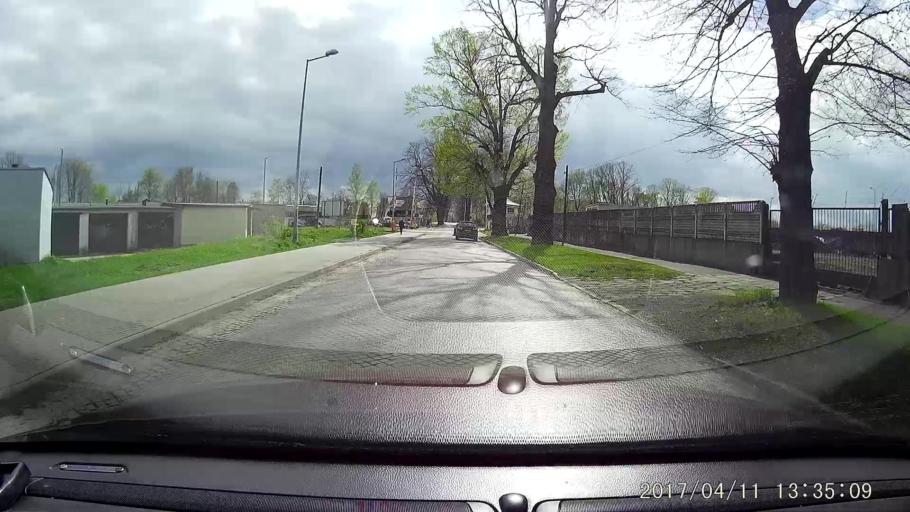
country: PL
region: Lower Silesian Voivodeship
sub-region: Powiat zgorzelecki
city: Zgorzelec
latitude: 51.1420
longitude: 15.0073
